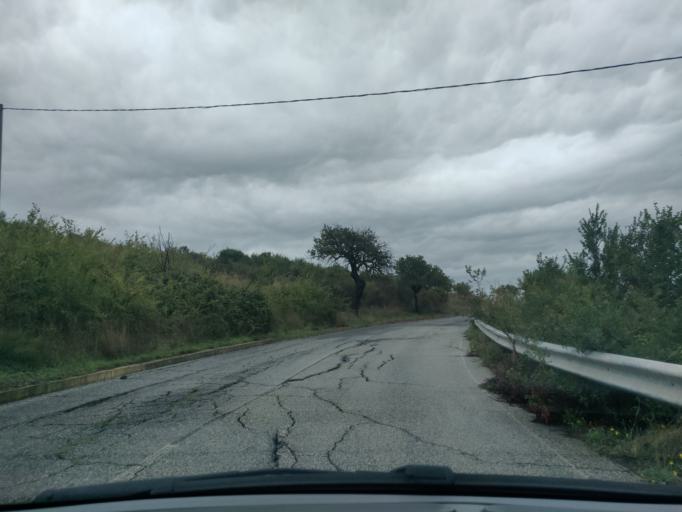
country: IT
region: Latium
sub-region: Citta metropolitana di Roma Capitale
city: Aurelia
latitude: 42.1306
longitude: 11.8470
